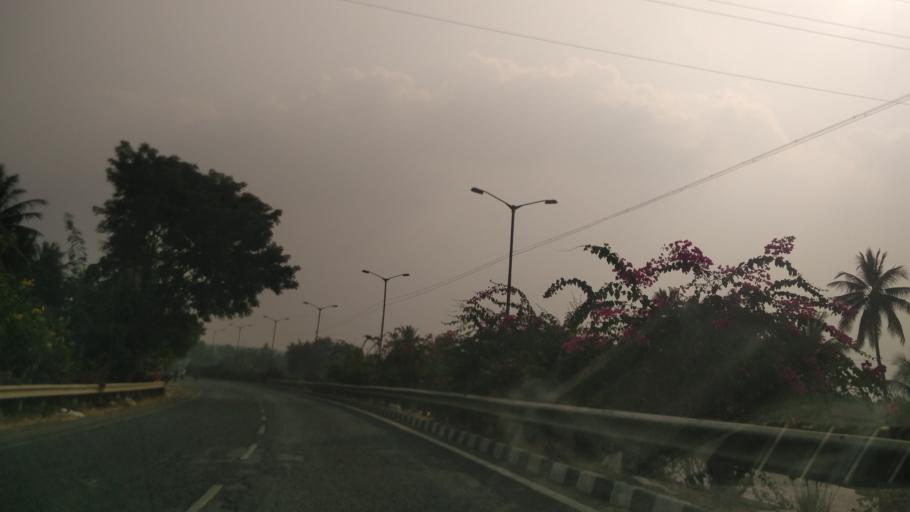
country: IN
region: Andhra Pradesh
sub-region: East Godavari
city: Rajahmundry
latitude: 16.9564
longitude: 81.7931
